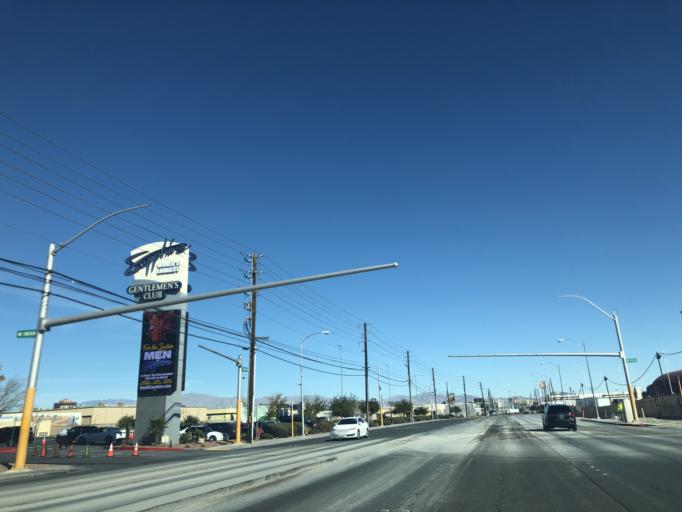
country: US
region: Nevada
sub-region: Clark County
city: Paradise
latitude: 36.1348
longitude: -115.1709
